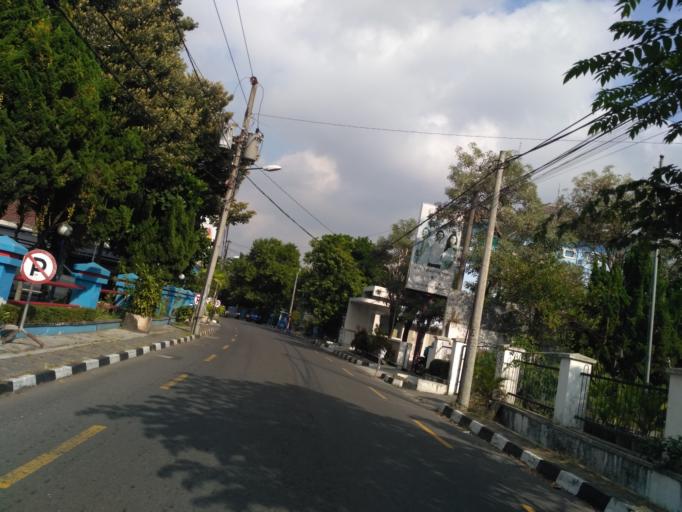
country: ID
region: Daerah Istimewa Yogyakarta
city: Yogyakarta
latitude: -7.7842
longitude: 110.3728
